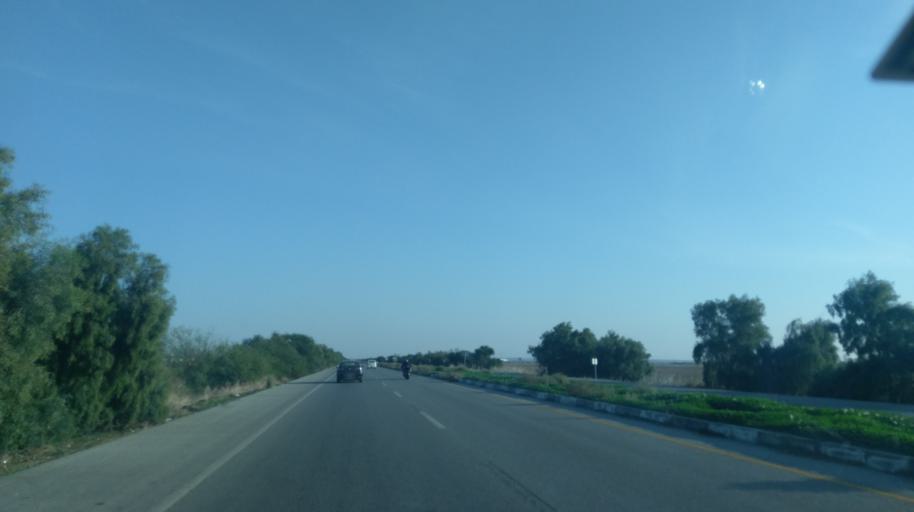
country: CY
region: Ammochostos
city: Acheritou
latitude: 35.1519
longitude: 33.8482
